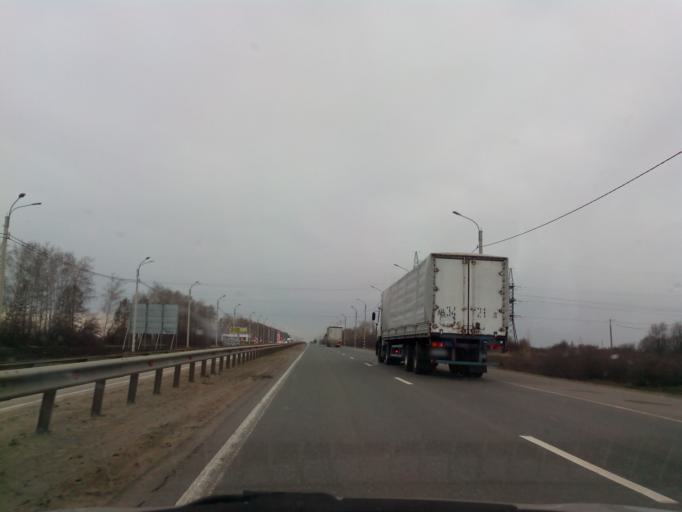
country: RU
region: Tambov
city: Komsomolets
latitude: 52.7350
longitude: 41.2806
